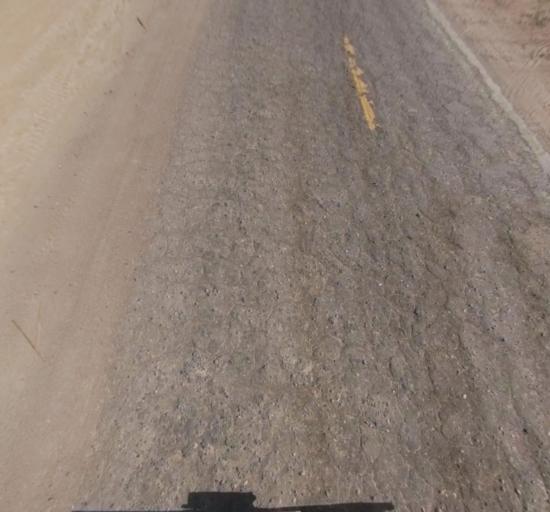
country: US
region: California
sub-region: Madera County
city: Parkwood
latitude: 36.8628
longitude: -120.1465
